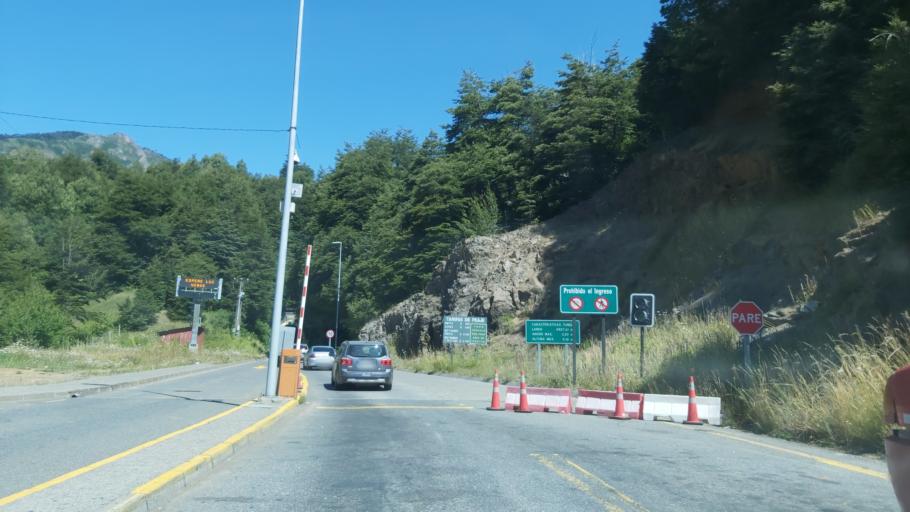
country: CL
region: Araucania
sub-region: Provincia de Cautin
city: Vilcun
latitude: -38.5167
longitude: -71.5170
